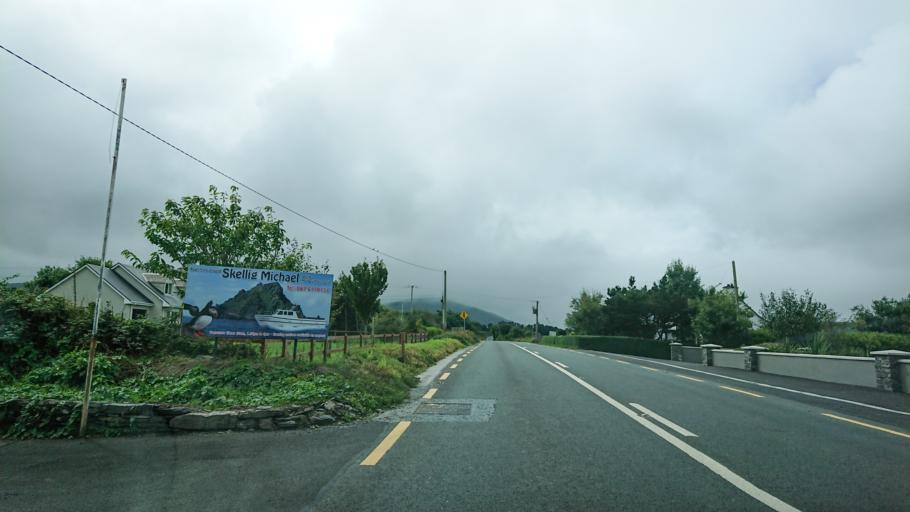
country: IE
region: Munster
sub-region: Ciarrai
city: Cahersiveen
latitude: 51.9617
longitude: -10.1819
